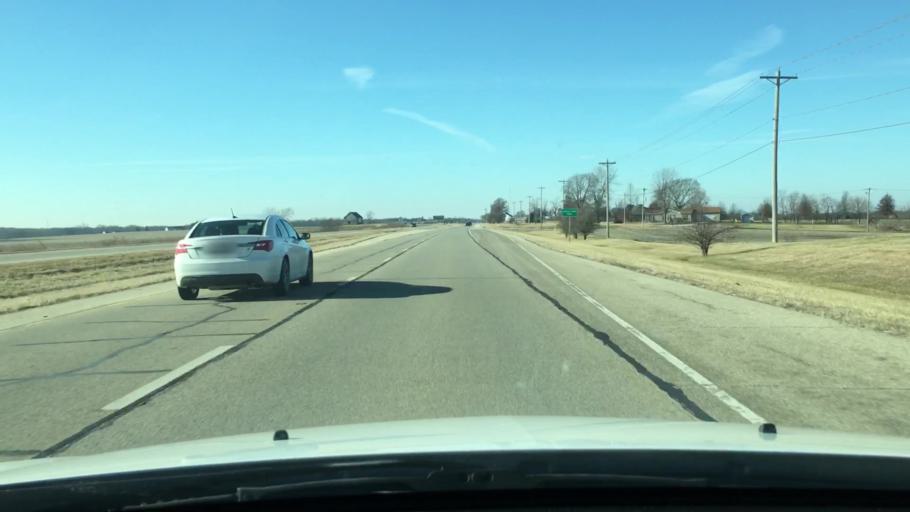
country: US
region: Illinois
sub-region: Woodford County
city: Germantown Hills
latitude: 40.7779
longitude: -89.4152
